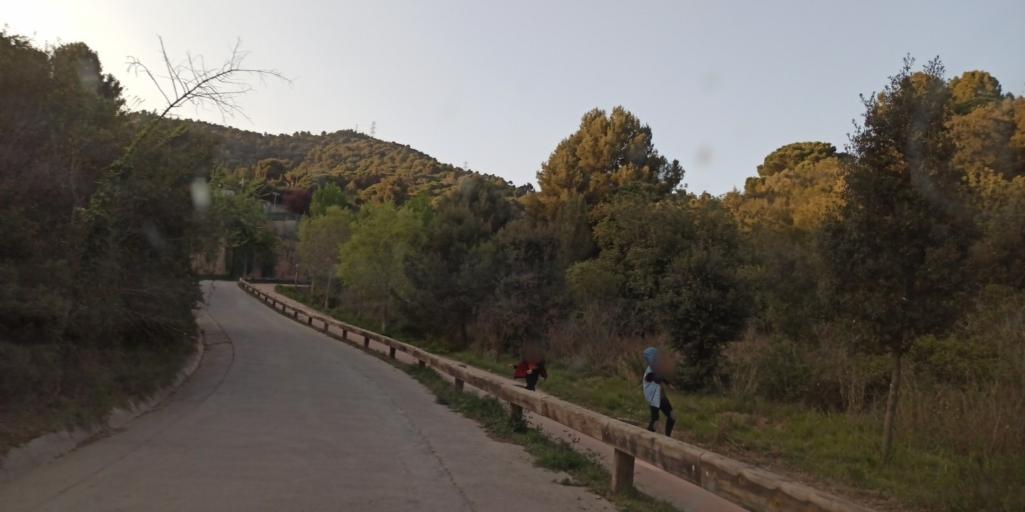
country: ES
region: Catalonia
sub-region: Provincia de Barcelona
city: Sant Just Desvern
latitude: 41.4024
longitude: 2.0877
